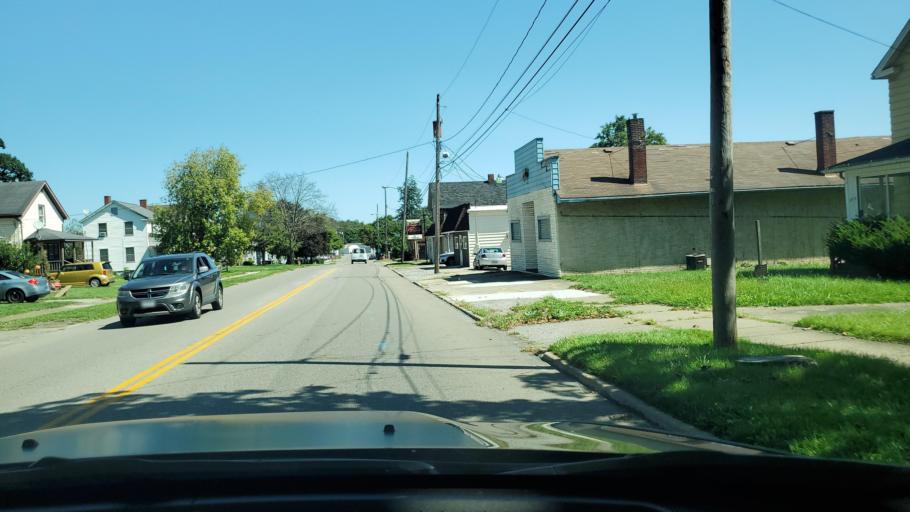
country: US
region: Ohio
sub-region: Mahoning County
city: Struthers
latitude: 41.0606
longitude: -80.6073
